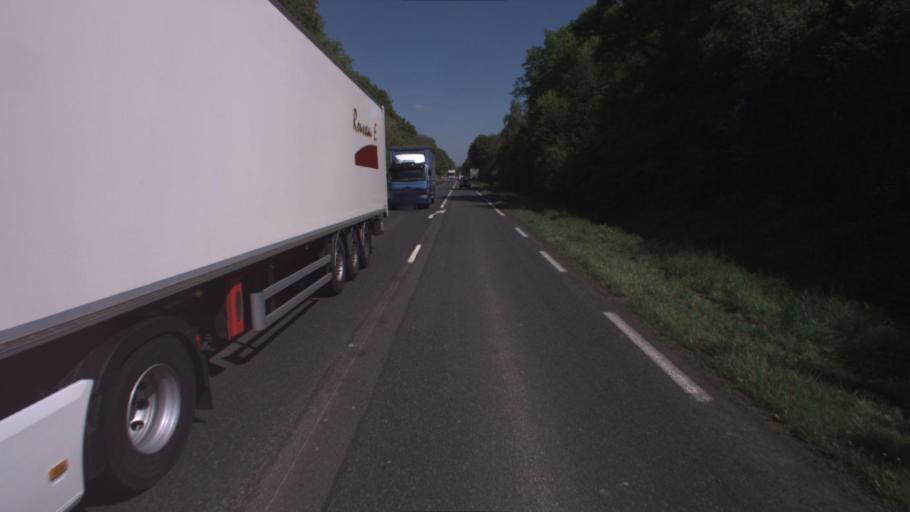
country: FR
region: Ile-de-France
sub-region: Departement de Seine-et-Marne
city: Voulangis
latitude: 48.8193
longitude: 2.8764
